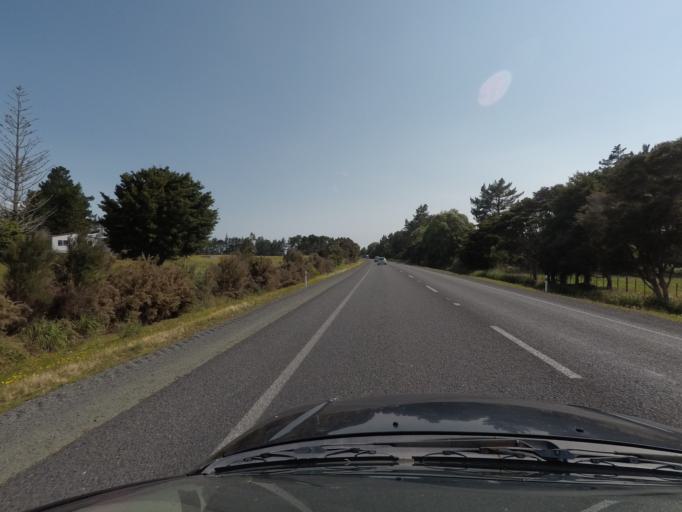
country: NZ
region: Northland
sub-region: Whangarei
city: Ruakaka
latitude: -35.9598
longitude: 174.4492
